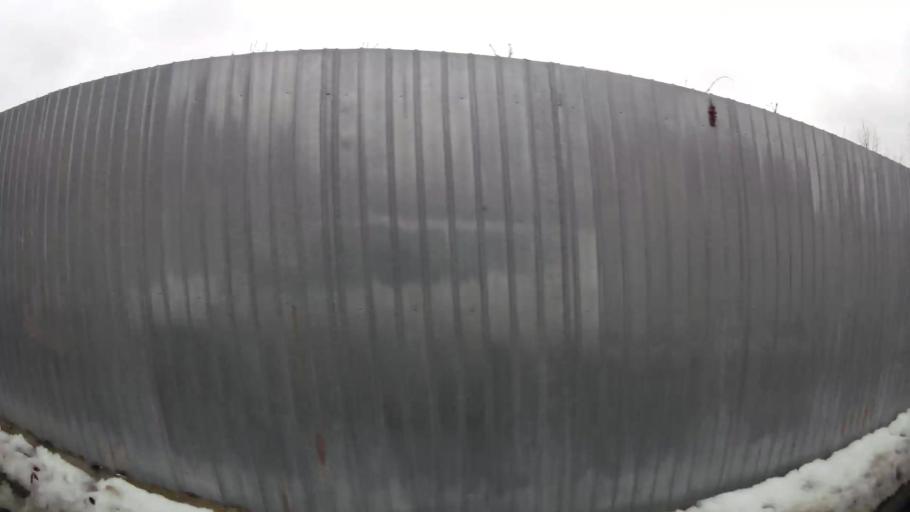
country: RO
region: Ilfov
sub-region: Comuna Otopeni
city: Otopeni
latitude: 44.5567
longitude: 26.0759
